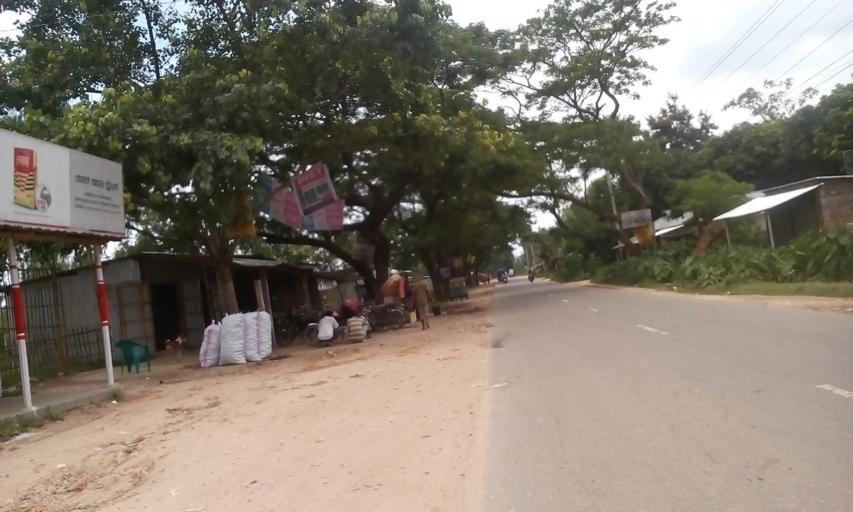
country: BD
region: Rangpur Division
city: Parbatipur
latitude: 25.3961
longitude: 88.9886
